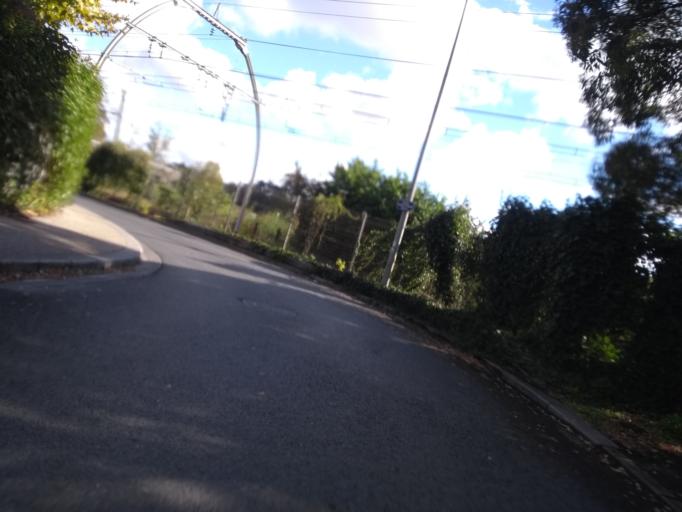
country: FR
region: Aquitaine
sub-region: Departement de la Gironde
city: Pessac
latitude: 44.8026
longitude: -0.6372
